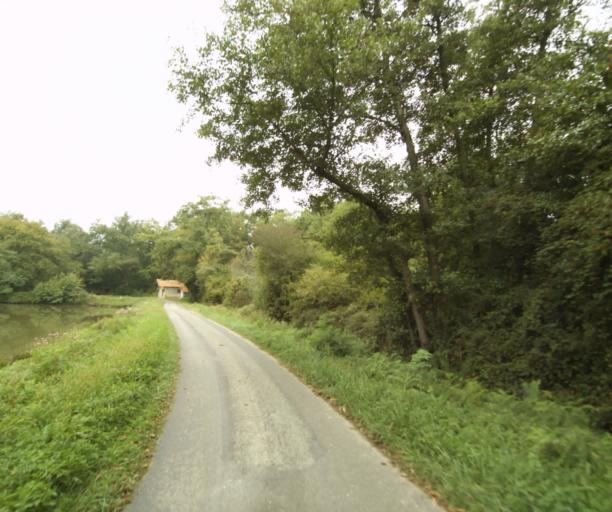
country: FR
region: Midi-Pyrenees
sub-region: Departement du Gers
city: Cazaubon
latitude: 43.9274
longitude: -0.1774
